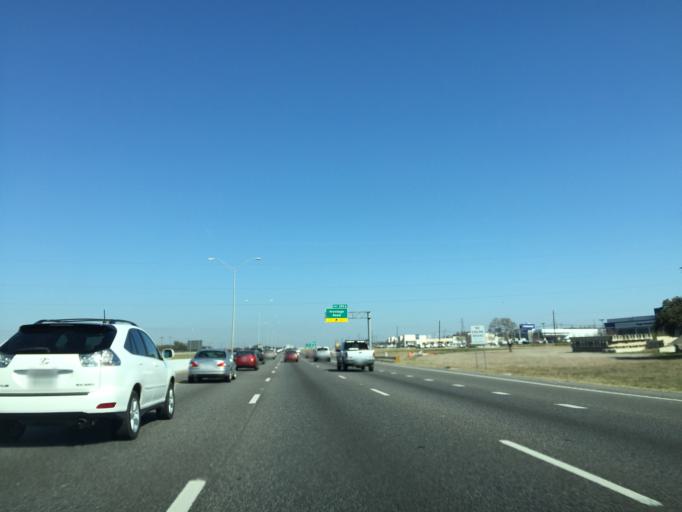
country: US
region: Texas
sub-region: Williamson County
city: Georgetown
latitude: 30.5776
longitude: -97.6928
